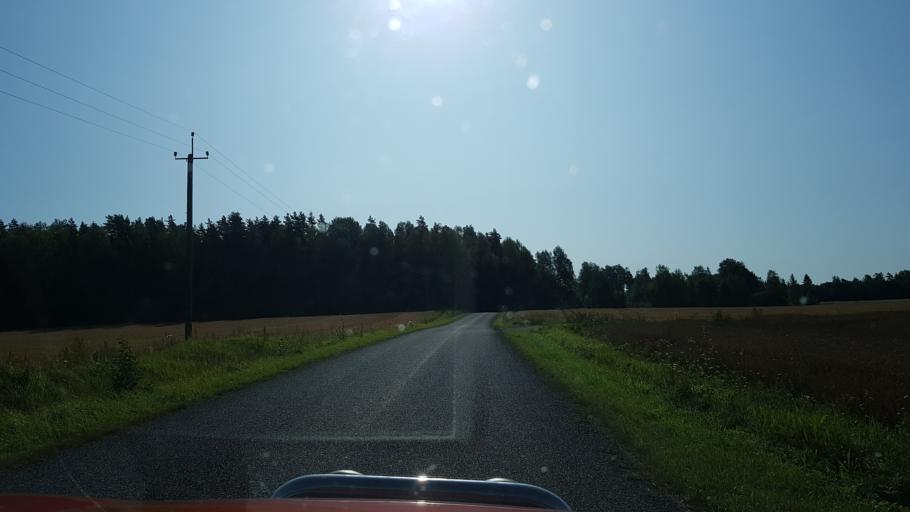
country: LV
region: Apes Novads
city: Ape
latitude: 57.6588
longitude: 26.7079
